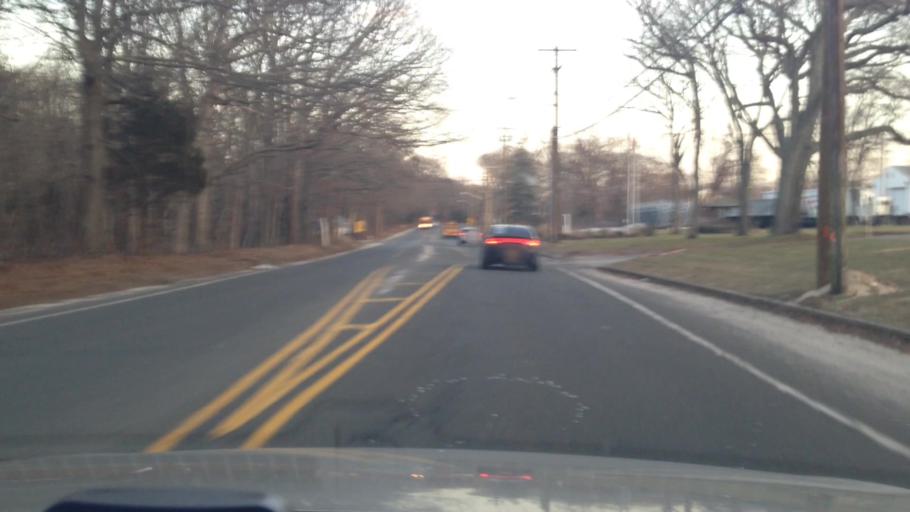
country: US
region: New York
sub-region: Suffolk County
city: Coram
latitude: 40.8726
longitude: -73.0132
